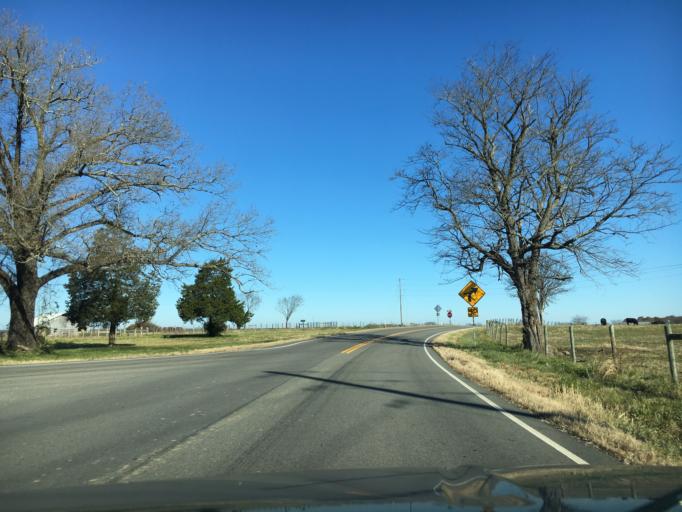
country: US
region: Virginia
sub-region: Buckingham County
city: Buckingham
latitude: 37.5367
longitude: -78.6149
